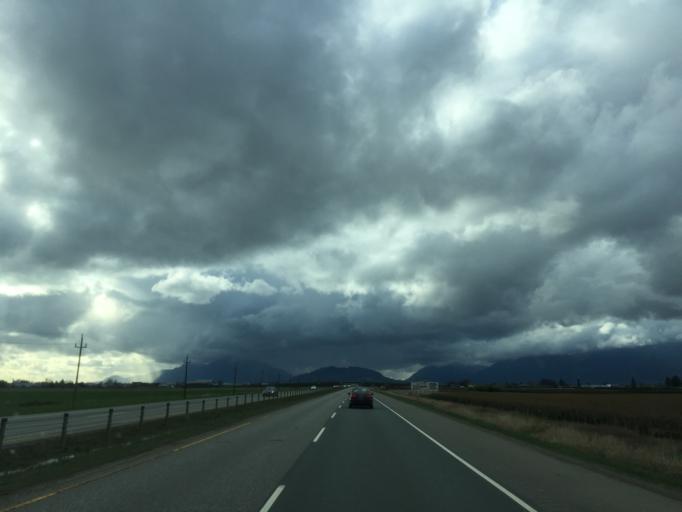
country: CA
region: British Columbia
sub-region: Fraser Valley Regional District
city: Chilliwack
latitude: 49.1551
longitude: -121.8592
